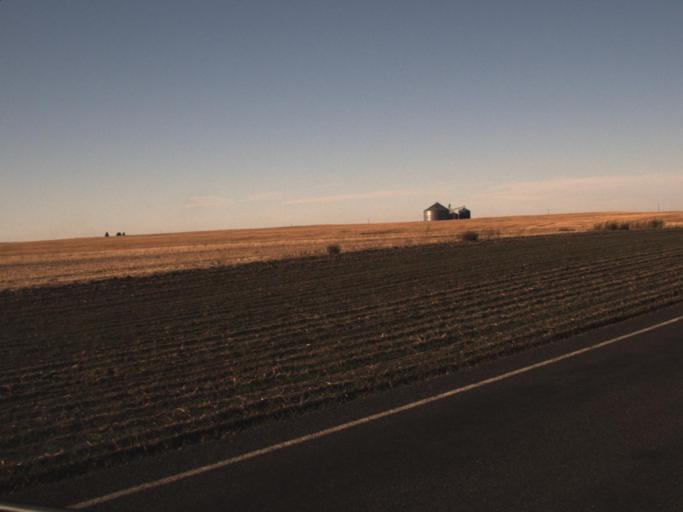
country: US
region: Washington
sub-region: Adams County
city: Ritzville
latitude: 46.8596
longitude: -118.3361
